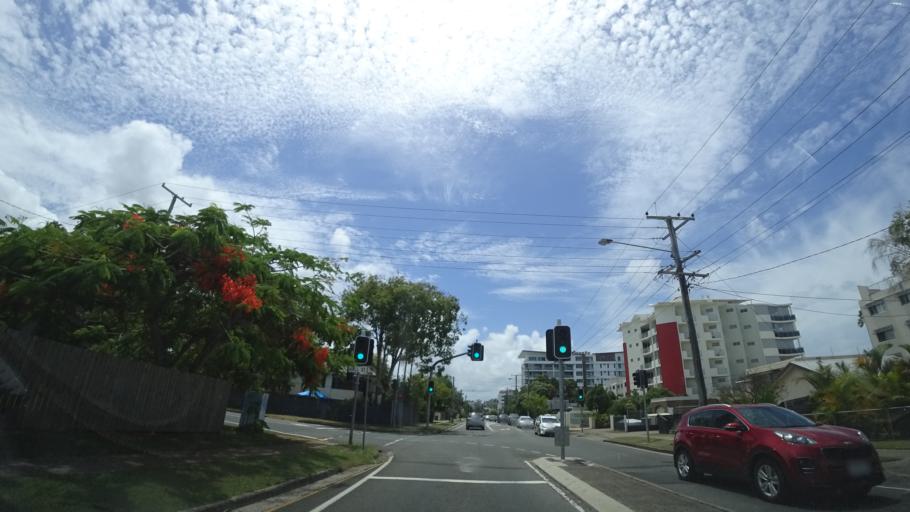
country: AU
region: Queensland
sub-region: Sunshine Coast
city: Mooloolaba
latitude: -26.6466
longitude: 153.0866
